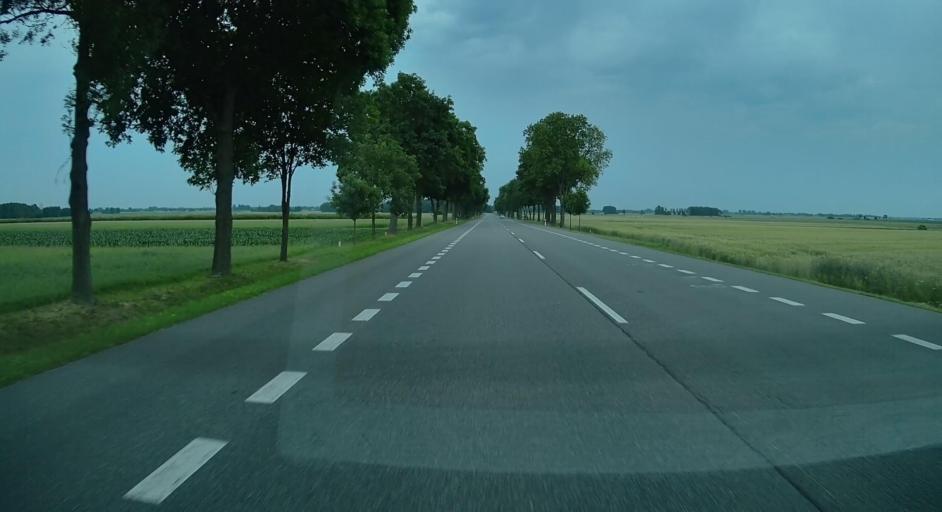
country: PL
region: Lublin Voivodeship
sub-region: Powiat lukowski
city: Trzebieszow
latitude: 52.0593
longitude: 22.5752
